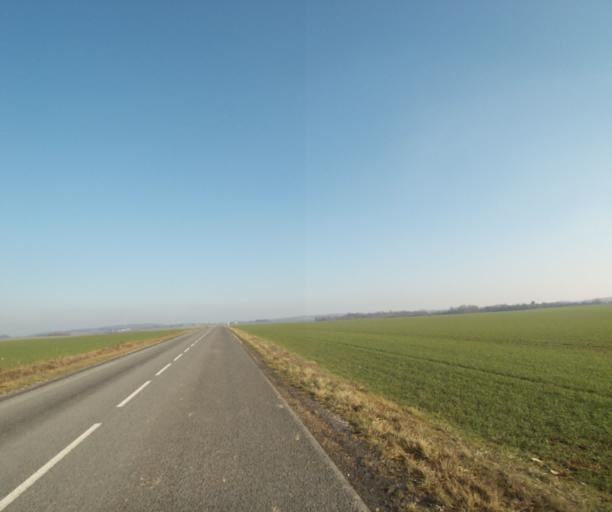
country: FR
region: Champagne-Ardenne
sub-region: Departement de la Haute-Marne
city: Wassy
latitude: 48.5034
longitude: 4.9691
